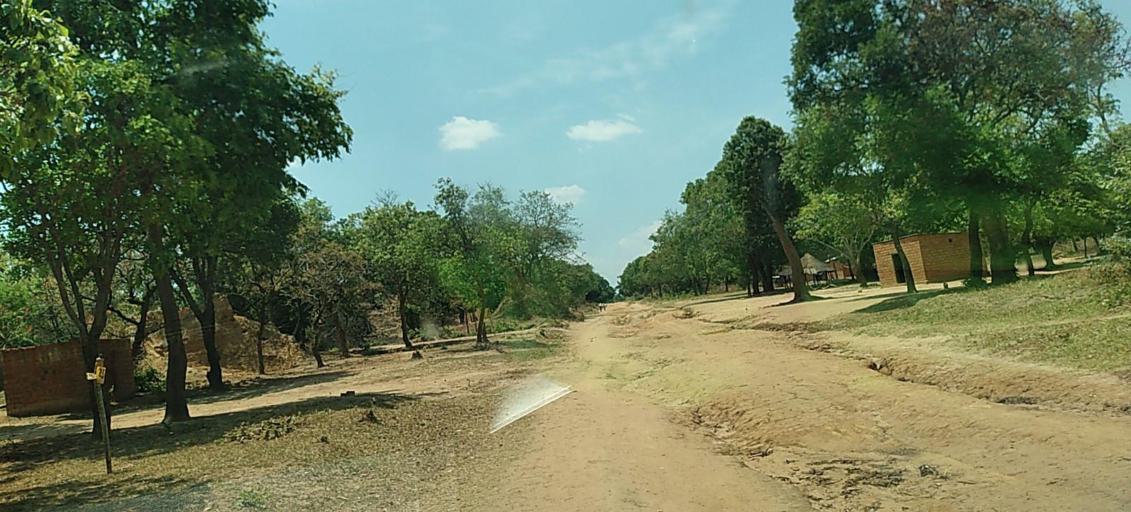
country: CD
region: Katanga
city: Kolwezi
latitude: -11.3235
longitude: 25.2288
